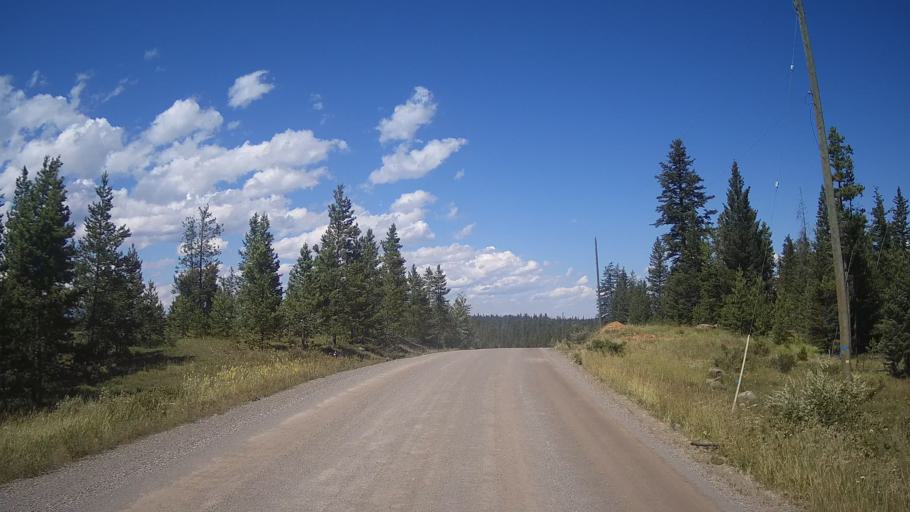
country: CA
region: British Columbia
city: Cache Creek
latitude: 51.2213
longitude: -121.6164
